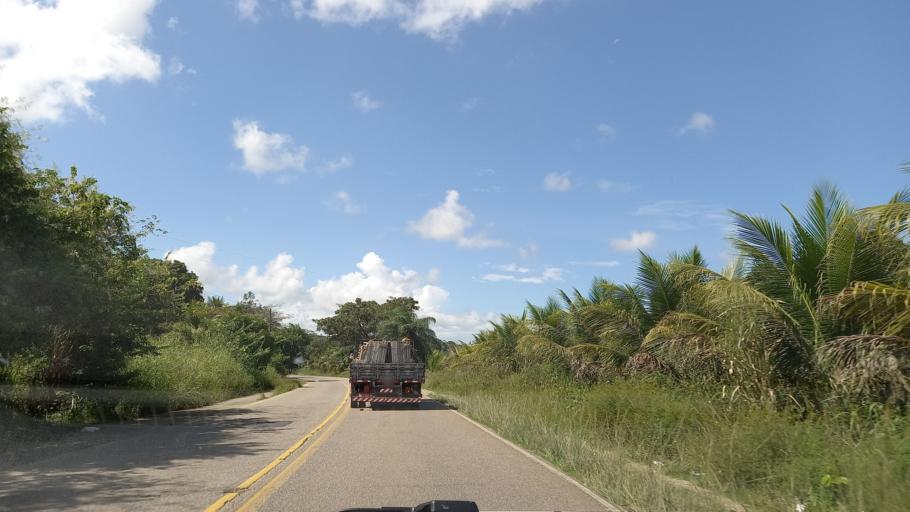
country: BR
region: Pernambuco
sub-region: Barreiros
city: Barreiros
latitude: -8.7810
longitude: -35.1755
